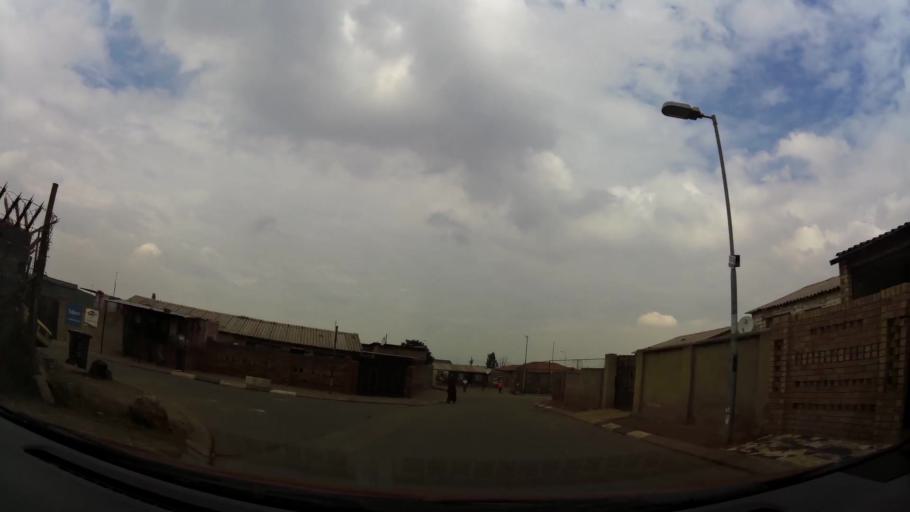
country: ZA
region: Gauteng
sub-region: City of Johannesburg Metropolitan Municipality
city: Soweto
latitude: -26.2557
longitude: 27.8267
